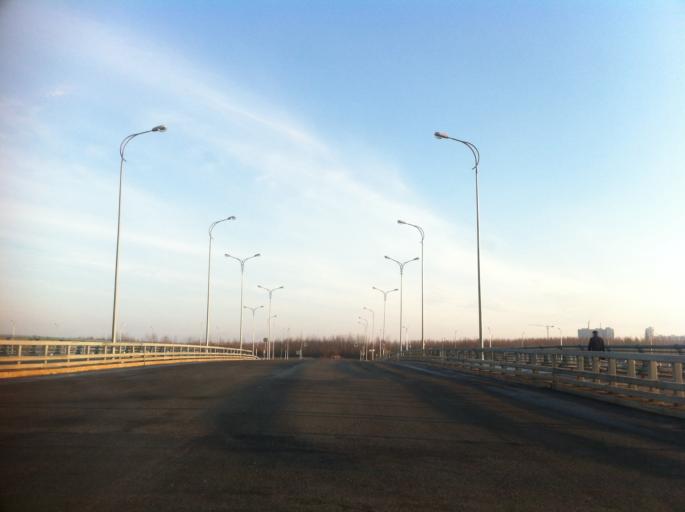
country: RU
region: St.-Petersburg
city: Sosnovaya Polyana
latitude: 59.8555
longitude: 30.1472
